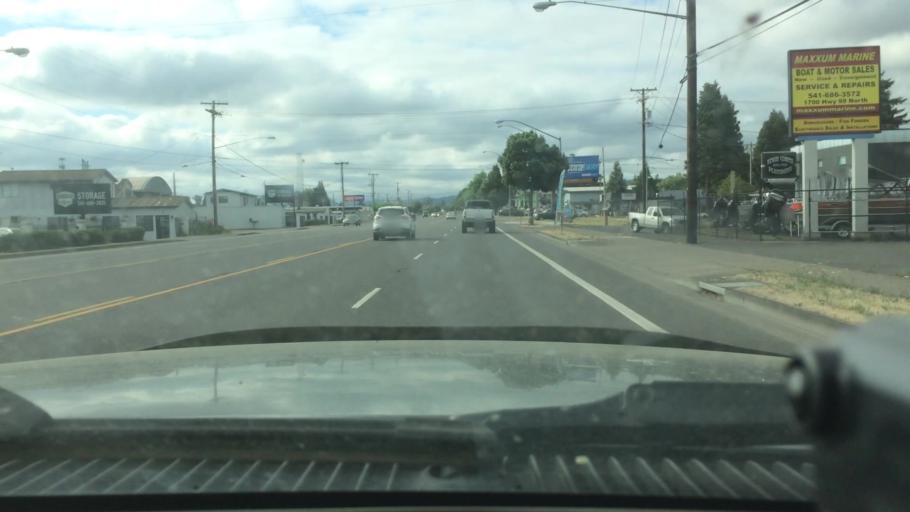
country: US
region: Oregon
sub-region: Lane County
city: Eugene
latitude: 44.0793
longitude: -123.1508
